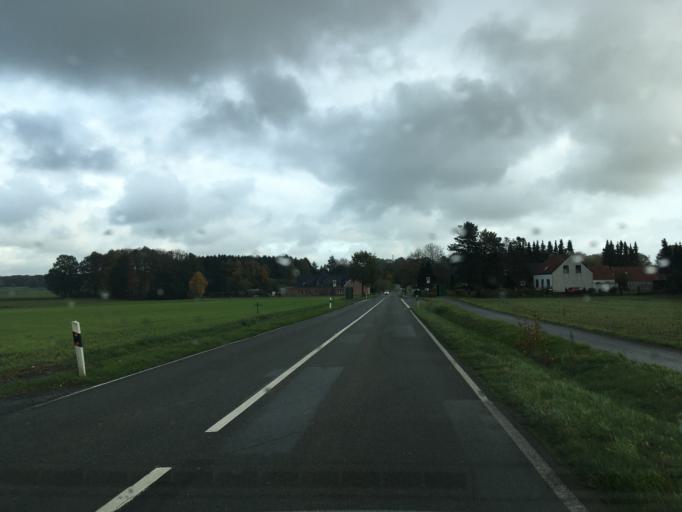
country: DE
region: North Rhine-Westphalia
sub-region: Regierungsbezirk Munster
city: Klein Reken
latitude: 51.8285
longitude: 7.0098
